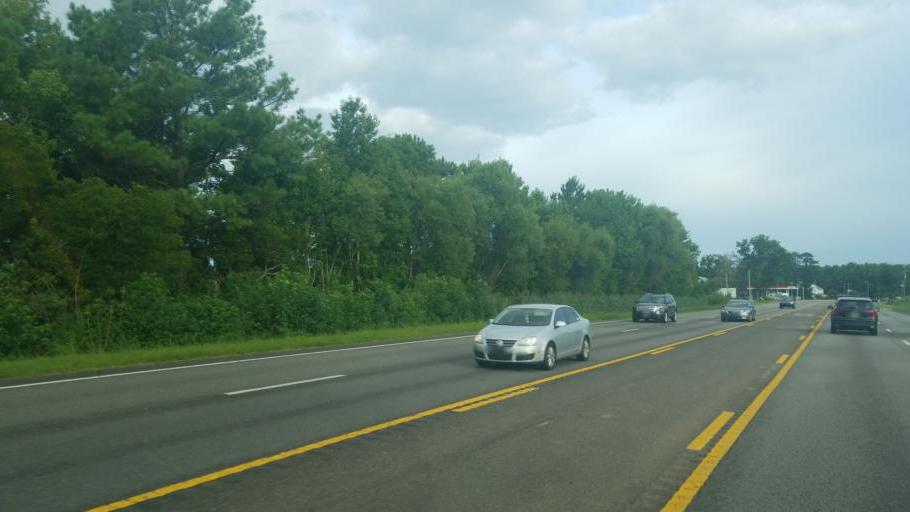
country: US
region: North Carolina
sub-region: Dare County
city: Southern Shores
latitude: 36.0937
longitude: -75.8097
